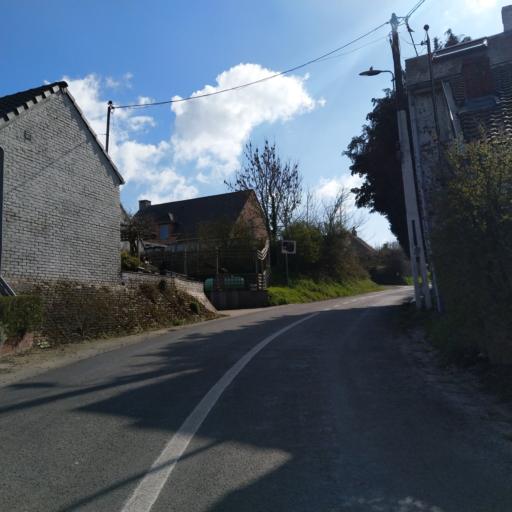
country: BE
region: Wallonia
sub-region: Province du Hainaut
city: Lens
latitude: 50.5828
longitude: 3.9130
